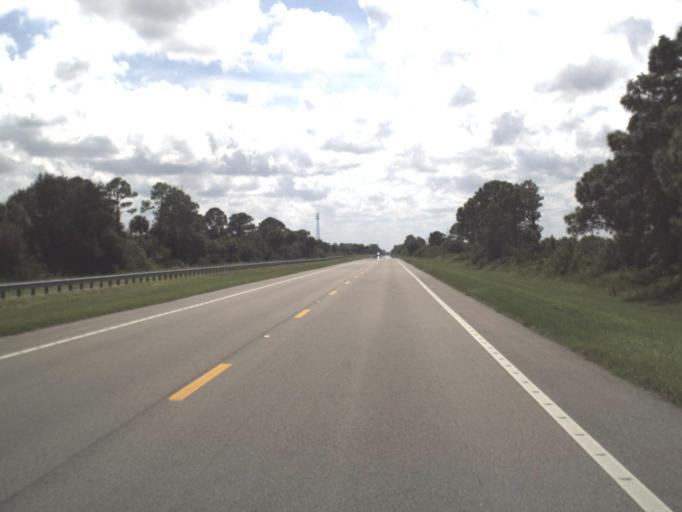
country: US
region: Florida
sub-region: Collier County
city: Immokalee
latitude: 26.3302
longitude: -81.3433
